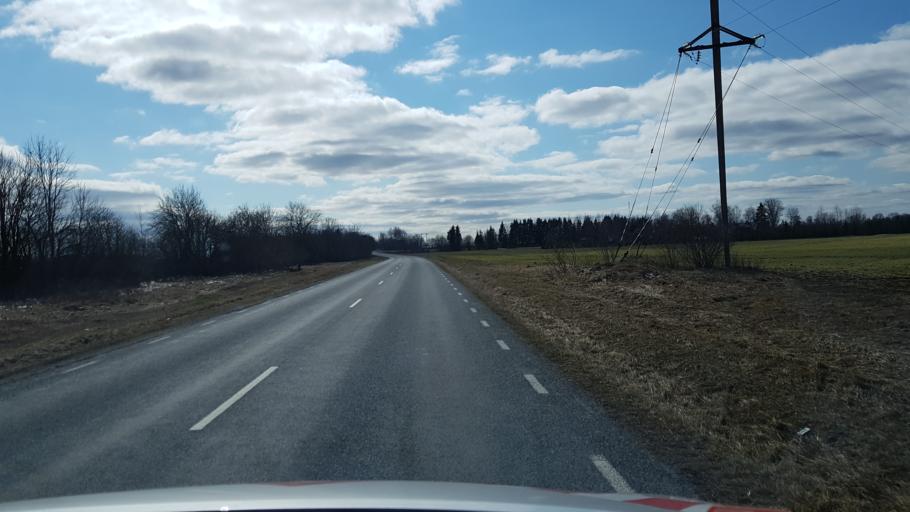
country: EE
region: Laeaene-Virumaa
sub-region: Tapa vald
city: Tapa
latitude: 59.2589
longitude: 25.8431
